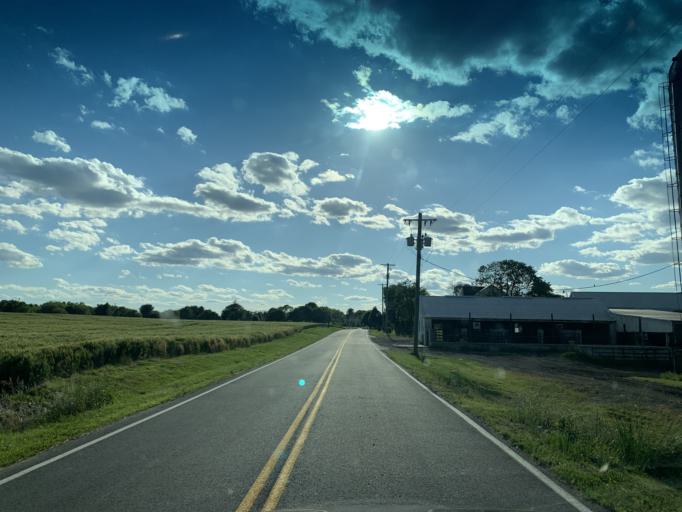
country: US
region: Maryland
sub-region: Cecil County
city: North East
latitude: 39.6756
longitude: -75.9586
